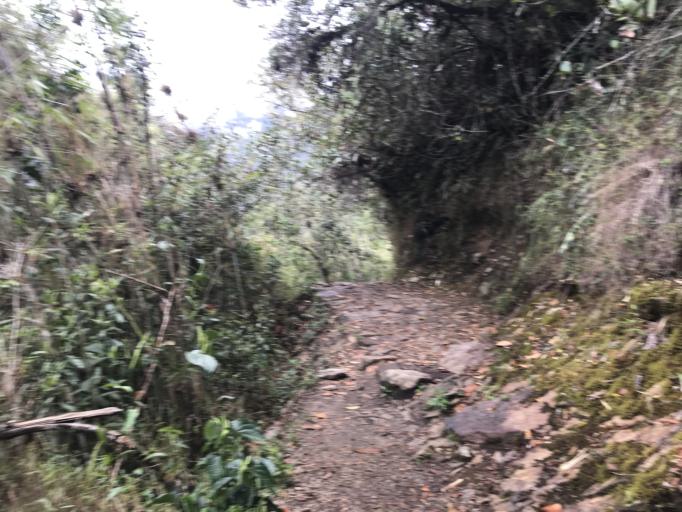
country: PE
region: Cusco
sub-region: Provincia de La Convencion
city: Santa Teresa
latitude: -13.1707
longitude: -72.5338
